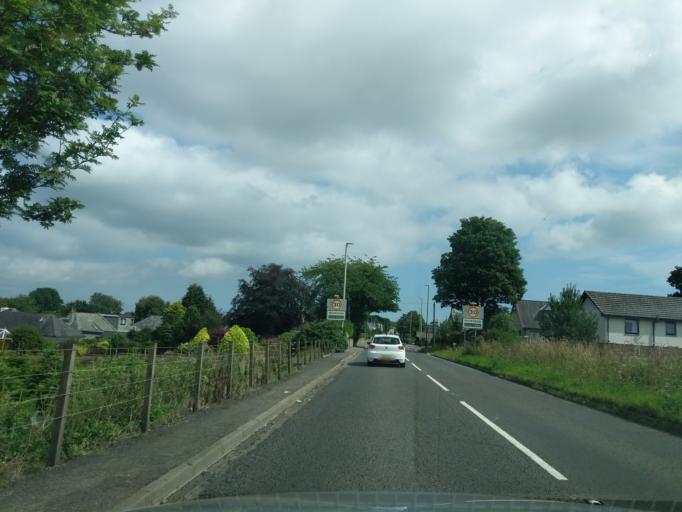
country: GB
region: Scotland
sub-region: Angus
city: Muirhead
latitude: 56.4981
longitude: -3.0734
